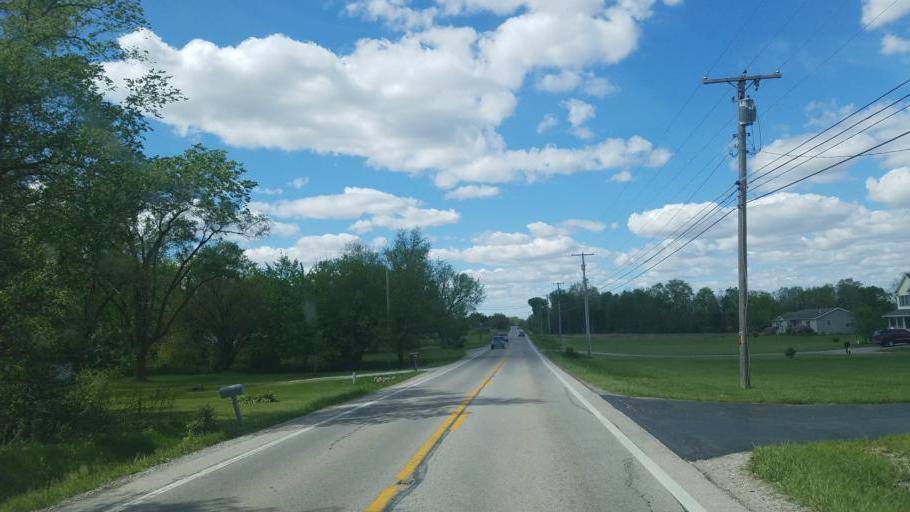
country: US
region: Ohio
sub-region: Marion County
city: Marion
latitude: 40.5108
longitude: -83.0969
